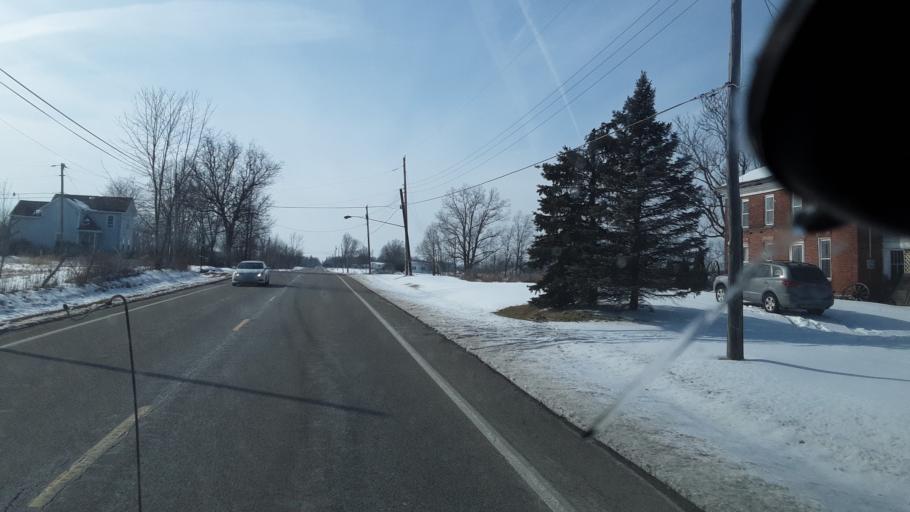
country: US
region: Ohio
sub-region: Mahoning County
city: Craig Beach
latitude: 41.0247
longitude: -81.0248
